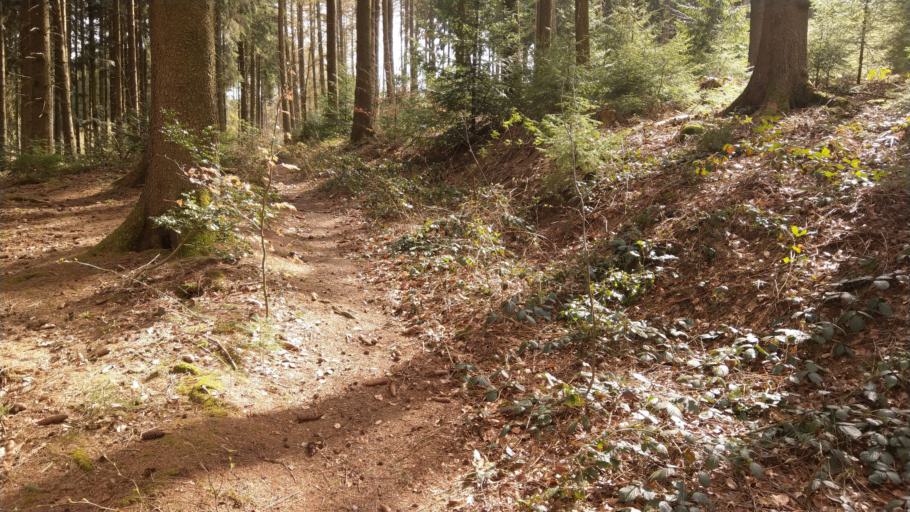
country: DE
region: North Rhine-Westphalia
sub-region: Regierungsbezirk Koln
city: Aachen
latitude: 50.7472
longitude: 6.0568
